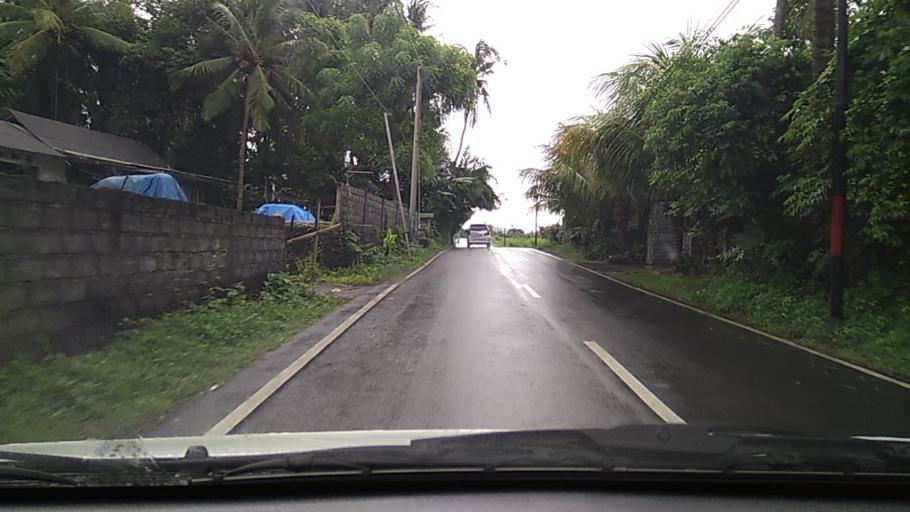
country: ID
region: Bali
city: Banjar Danginsema
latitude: -8.4678
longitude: 115.6189
